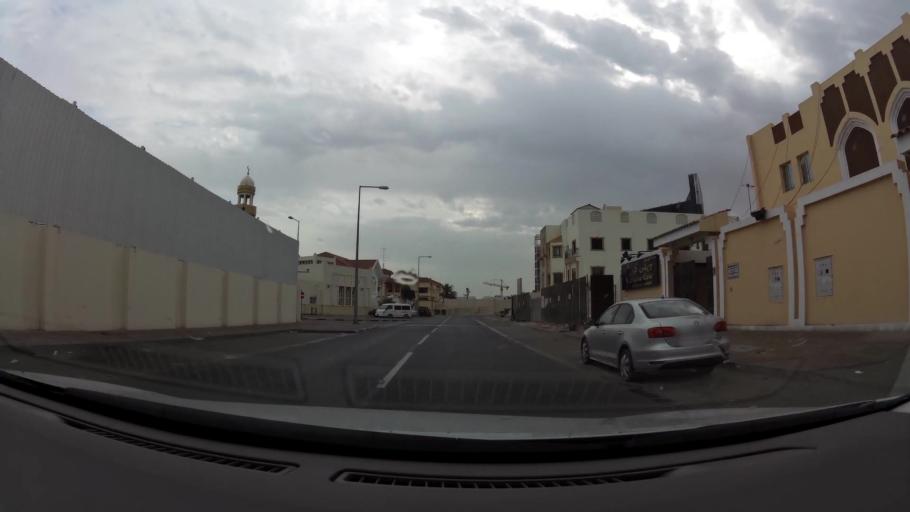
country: QA
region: Baladiyat ad Dawhah
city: Doha
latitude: 25.2760
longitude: 51.4914
